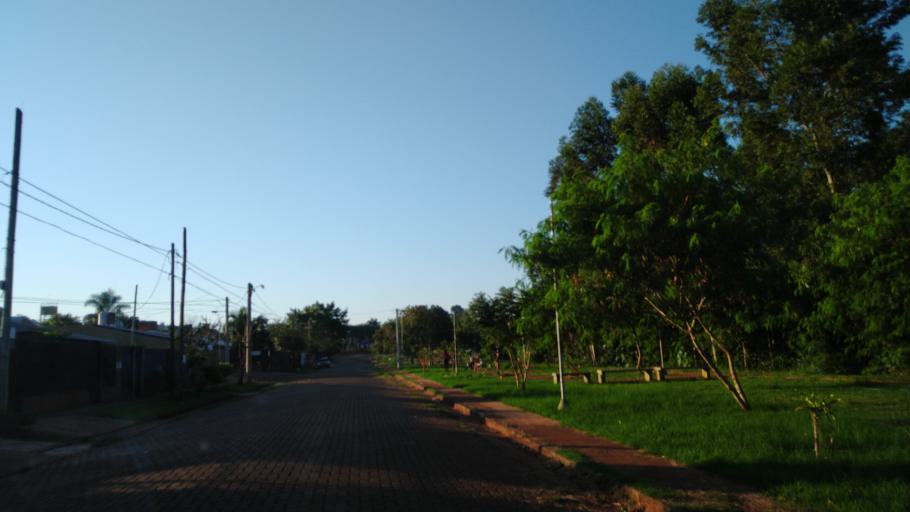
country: AR
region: Misiones
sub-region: Departamento de Capital
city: Posadas
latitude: -27.4326
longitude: -55.9244
